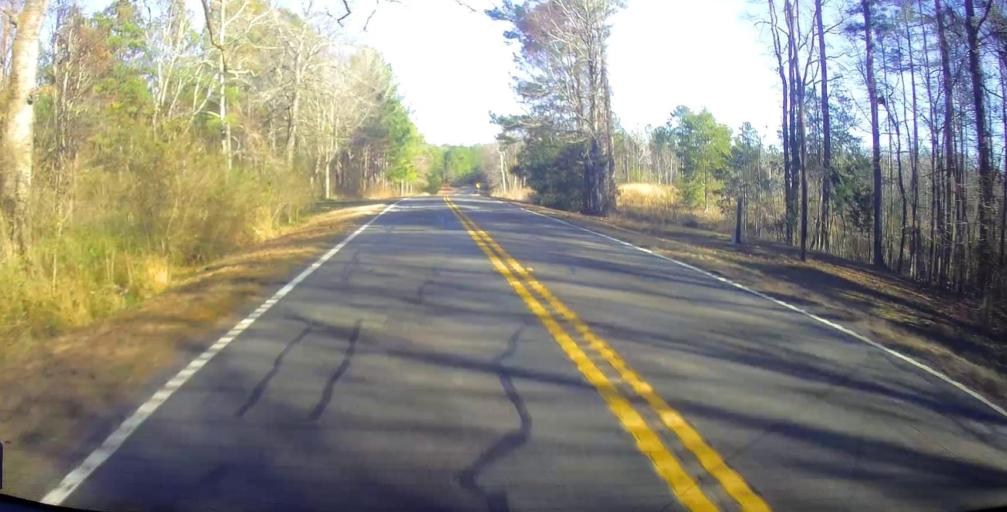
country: US
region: Georgia
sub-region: Talbot County
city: Talbotton
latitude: 32.6506
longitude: -84.4479
